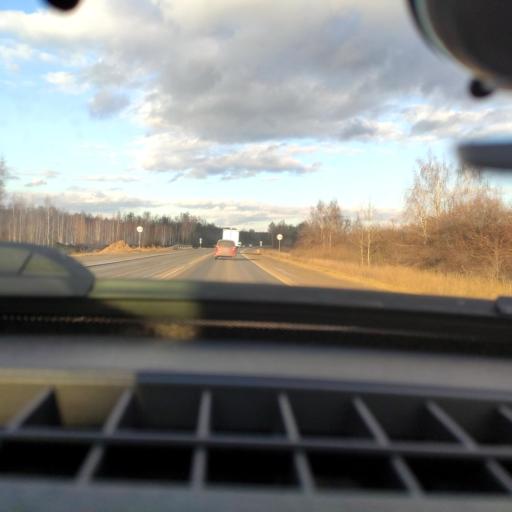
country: RU
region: Bashkortostan
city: Kabakovo
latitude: 54.7182
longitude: 56.2355
